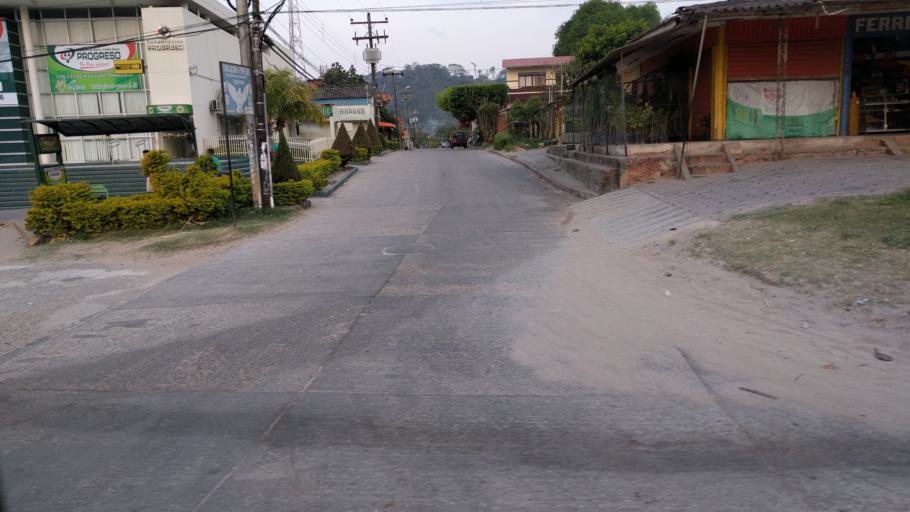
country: BO
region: Santa Cruz
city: Santiago del Torno
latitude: -17.9909
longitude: -63.3814
